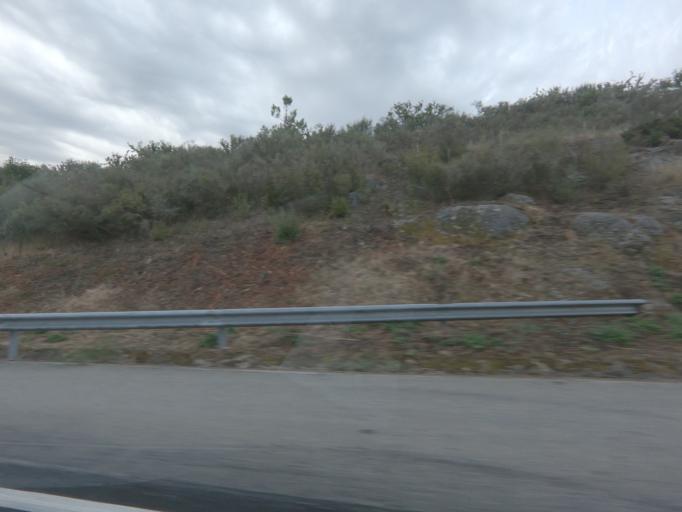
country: PT
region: Viseu
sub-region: Lamego
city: Lamego
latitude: 41.0779
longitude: -7.8042
